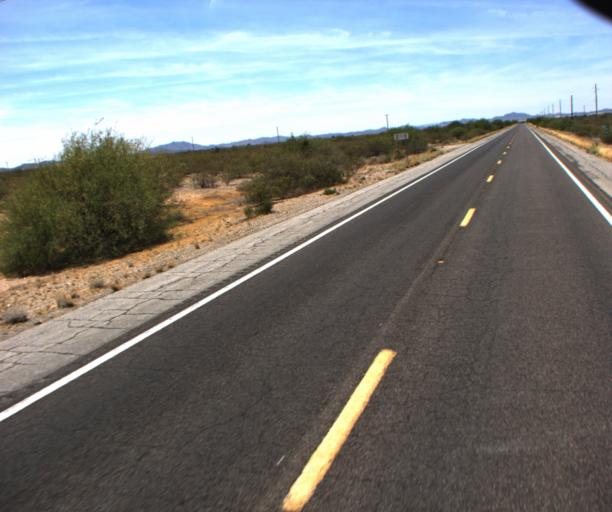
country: US
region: Arizona
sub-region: La Paz County
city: Salome
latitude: 33.8328
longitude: -113.5011
